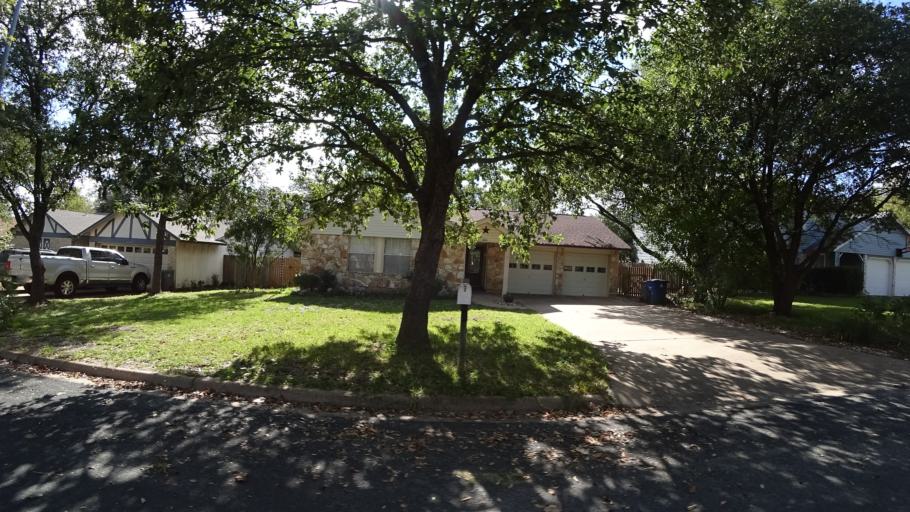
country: US
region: Texas
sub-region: Travis County
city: Wells Branch
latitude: 30.4157
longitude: -97.7205
